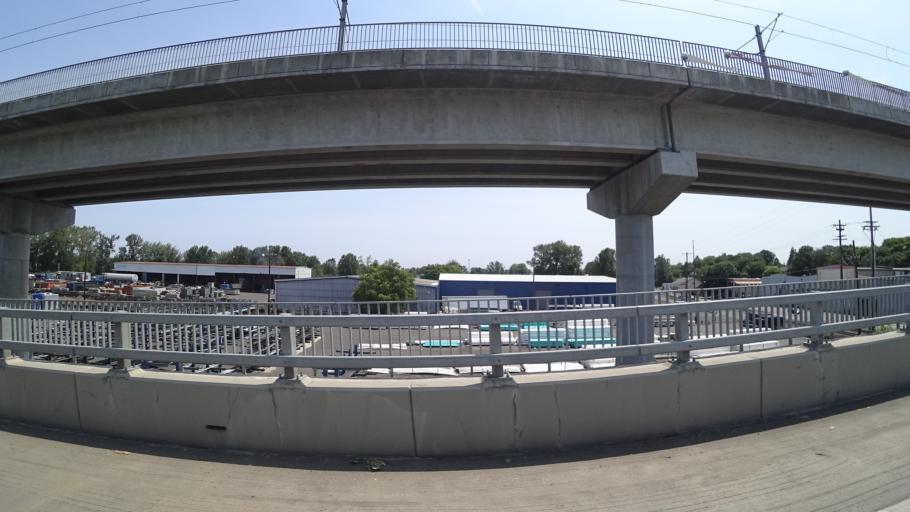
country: US
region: Washington
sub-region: Clark County
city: Vancouver
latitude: 45.5864
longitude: -122.6869
